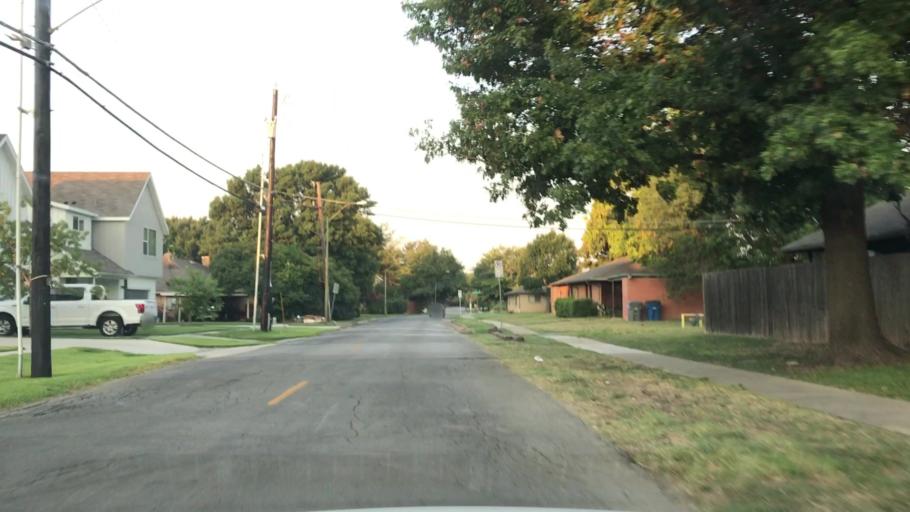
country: US
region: Texas
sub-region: Dallas County
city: Highland Park
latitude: 32.8537
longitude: -96.7473
